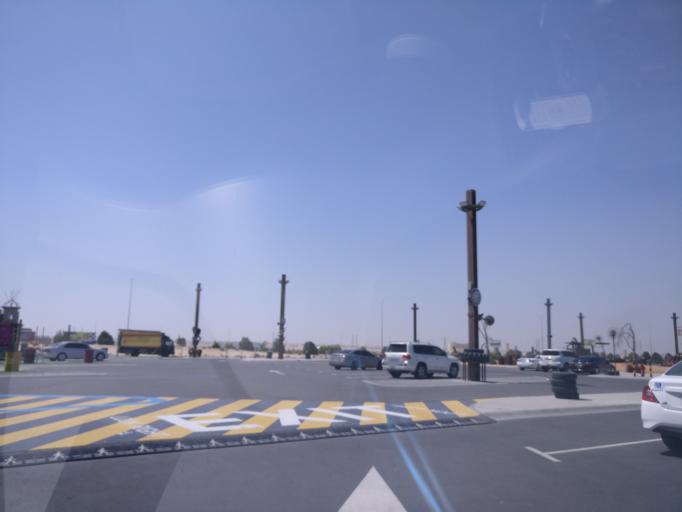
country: AE
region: Dubai
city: Dubai
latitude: 24.9140
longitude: 54.9611
